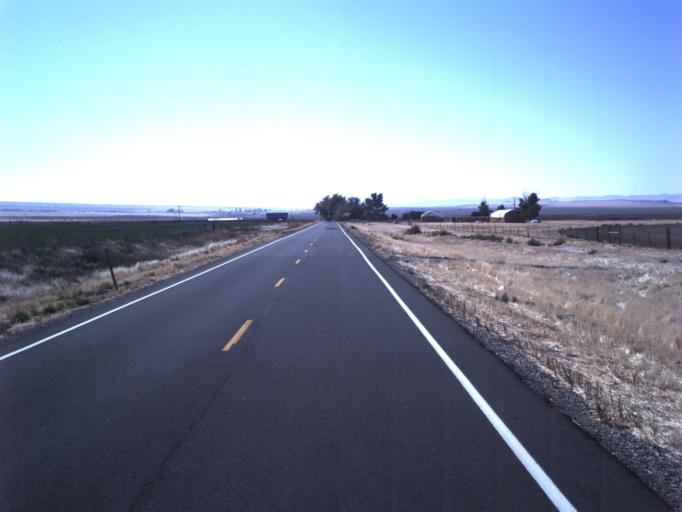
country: US
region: Utah
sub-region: Tooele County
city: Grantsville
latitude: 40.4997
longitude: -112.7480
